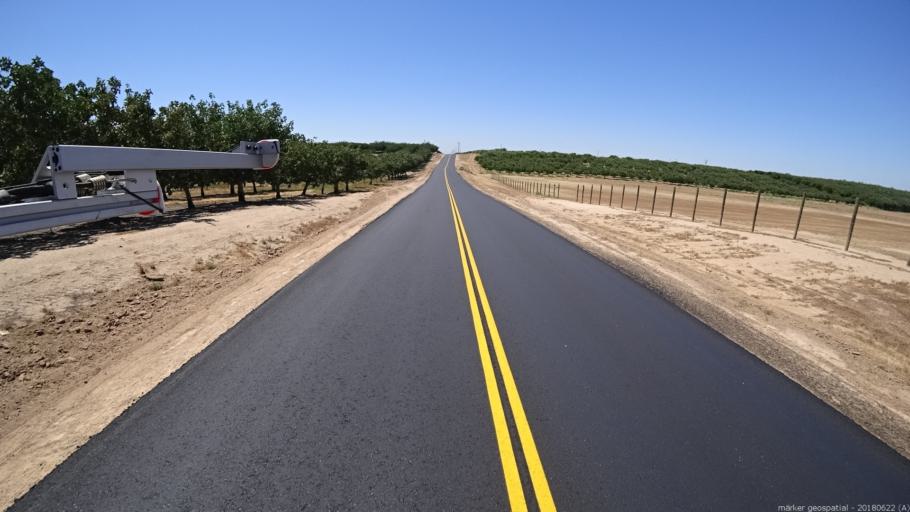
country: US
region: California
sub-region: Madera County
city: Bonadelle Ranchos-Madera Ranchos
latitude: 36.9049
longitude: -119.8576
